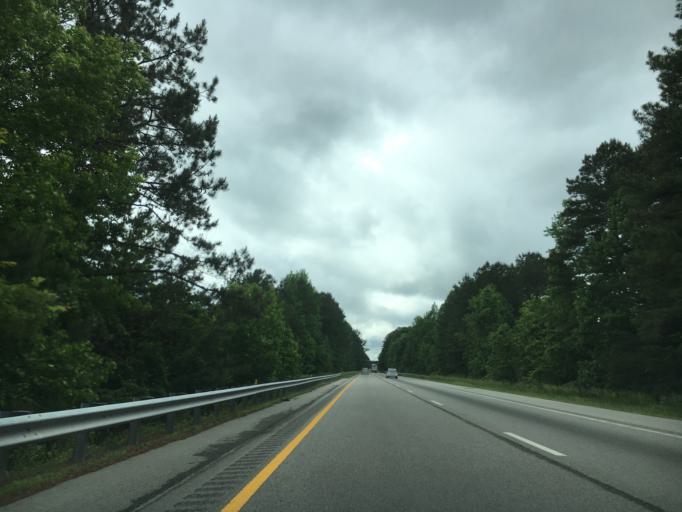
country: US
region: Virginia
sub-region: Mecklenburg County
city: South Hill
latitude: 36.7725
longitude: -78.0431
